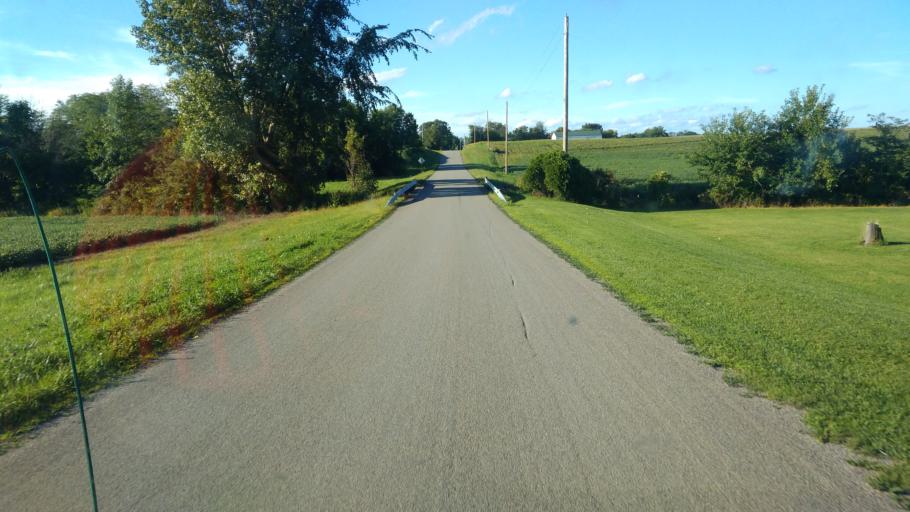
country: US
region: Ohio
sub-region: Wyandot County
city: Upper Sandusky
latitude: 40.8033
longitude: -83.3808
